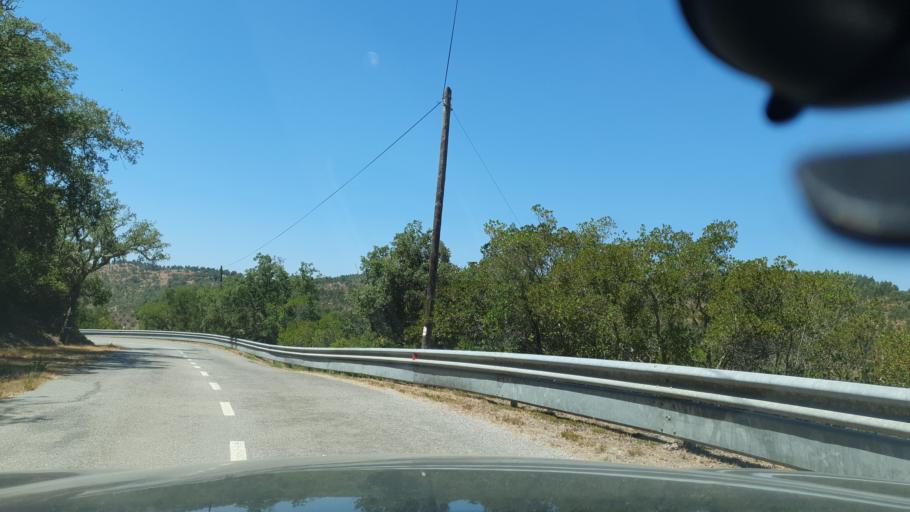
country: PT
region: Beja
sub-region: Odemira
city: Odemira
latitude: 37.6024
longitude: -8.5706
